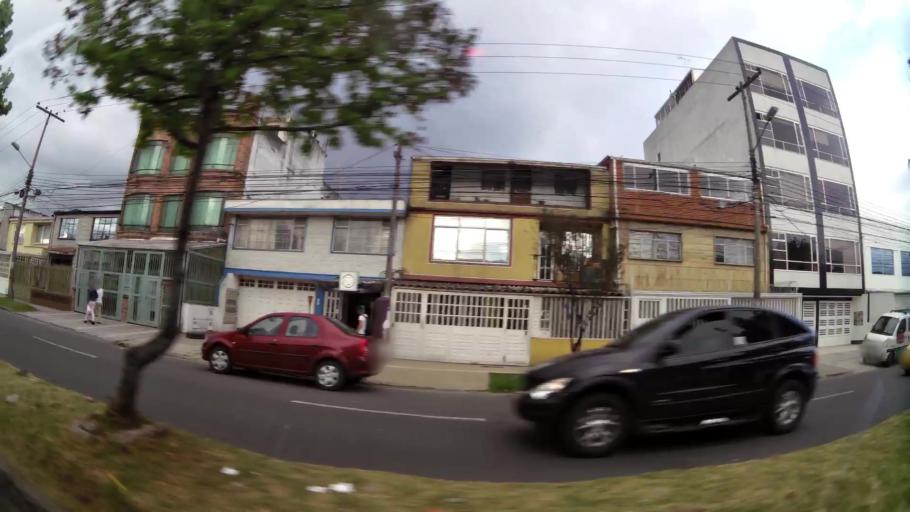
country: CO
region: Bogota D.C.
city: Bogota
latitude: 4.6009
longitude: -74.1004
